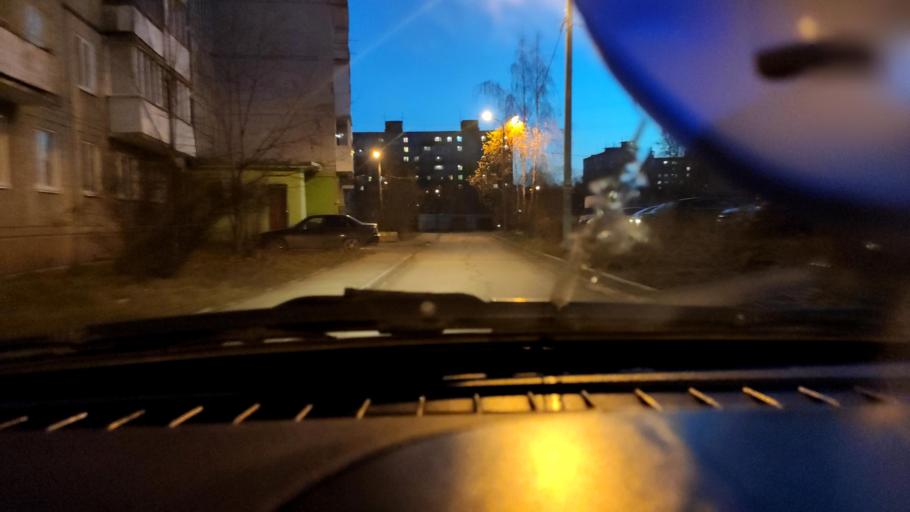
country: RU
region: Perm
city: Perm
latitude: 57.9645
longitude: 56.2339
